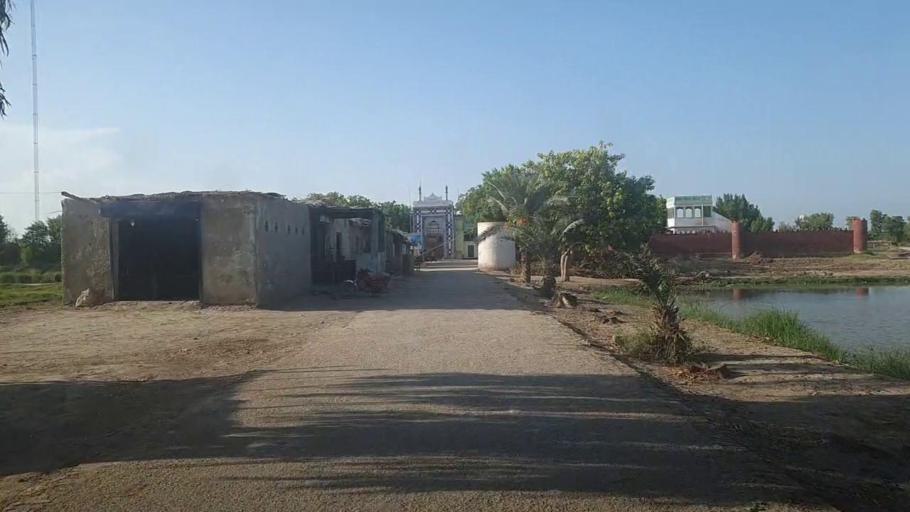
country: PK
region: Sindh
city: Khairpur
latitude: 28.1132
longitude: 69.6376
